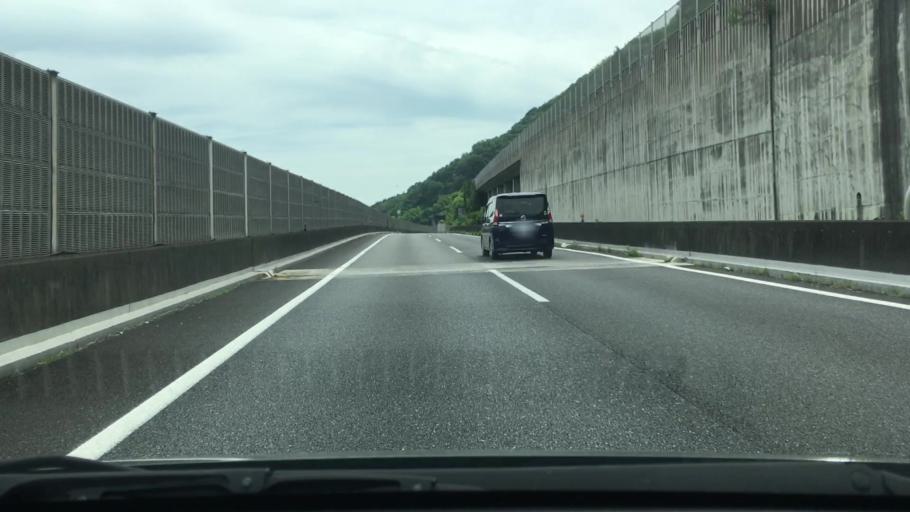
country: JP
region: Yamaguchi
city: Otake
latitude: 34.2224
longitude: 132.2009
